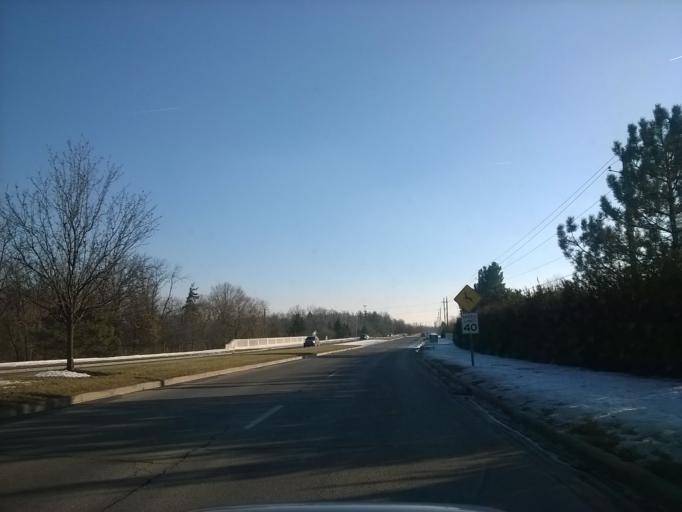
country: US
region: Indiana
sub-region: Hamilton County
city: Carmel
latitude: 39.9550
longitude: -86.0737
